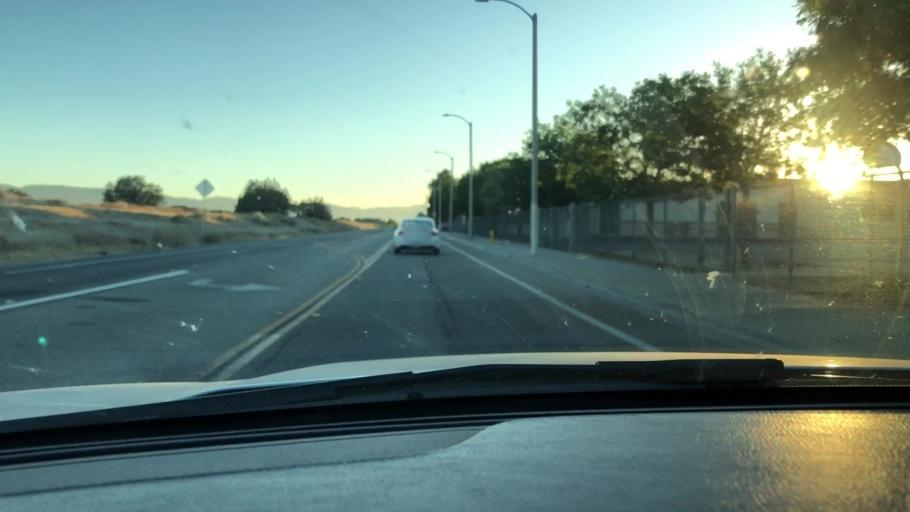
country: US
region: California
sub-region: Los Angeles County
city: Quartz Hill
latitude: 34.6822
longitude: -118.1931
